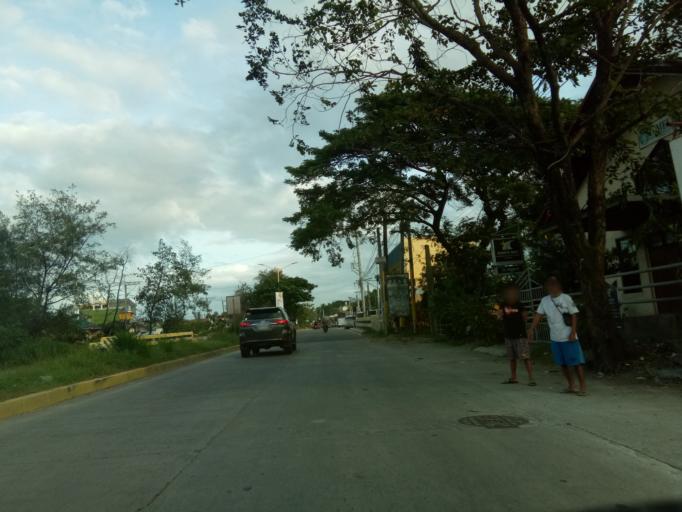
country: PH
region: Calabarzon
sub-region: Province of Cavite
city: Imus
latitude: 14.3874
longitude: 120.9722
